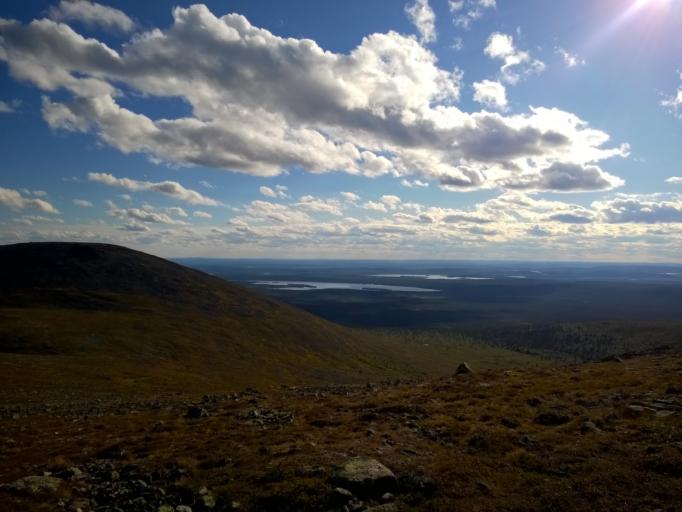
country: FI
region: Lapland
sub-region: Tunturi-Lappi
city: Muonio
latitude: 68.0719
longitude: 24.0480
